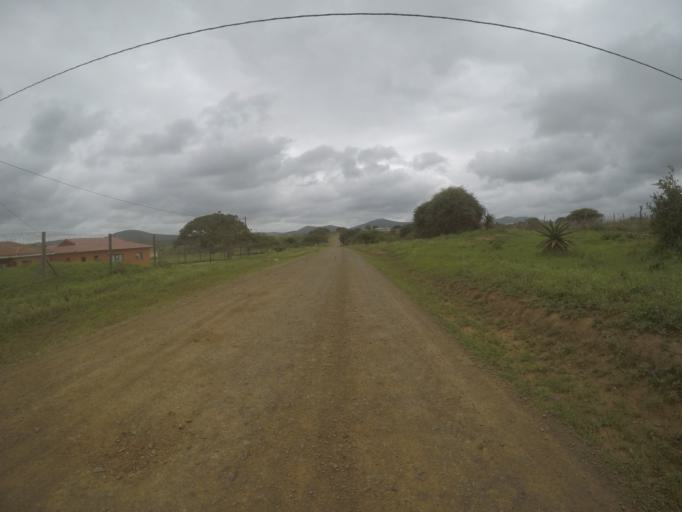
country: ZA
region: KwaZulu-Natal
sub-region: uThungulu District Municipality
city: Empangeni
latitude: -28.6030
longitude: 31.8699
